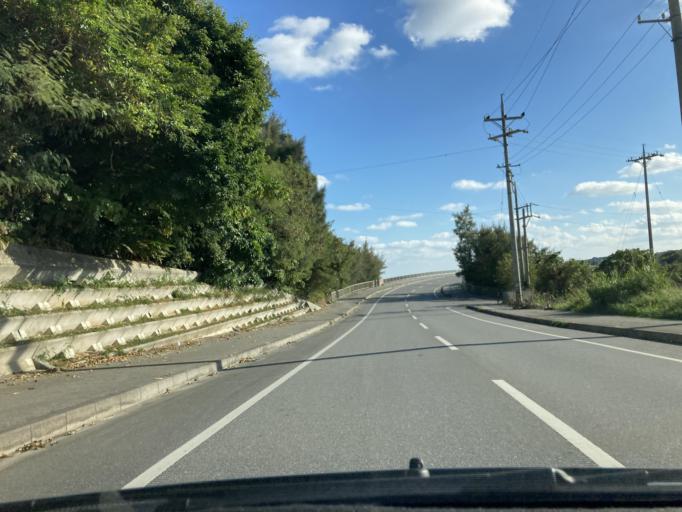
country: JP
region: Okinawa
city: Katsuren-haebaru
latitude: 26.3181
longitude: 127.9180
